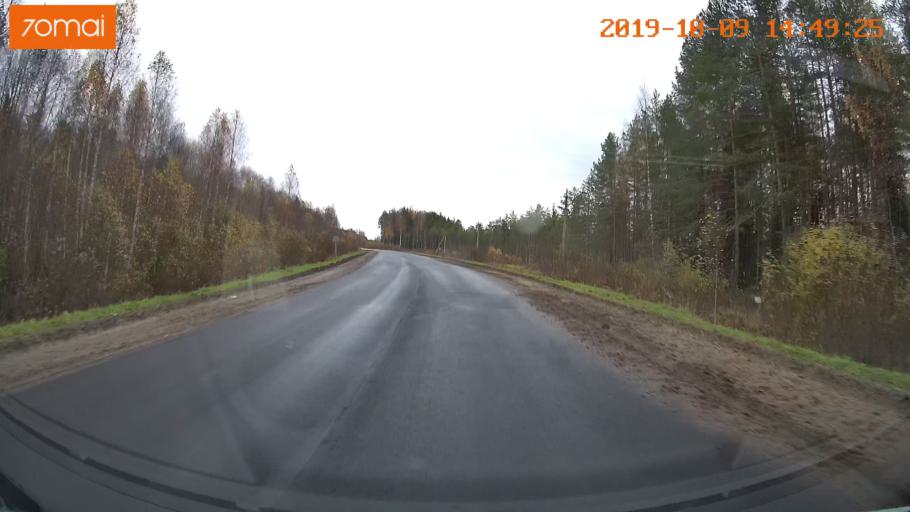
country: RU
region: Kostroma
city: Chistyye Bory
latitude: 58.3935
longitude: 41.5817
